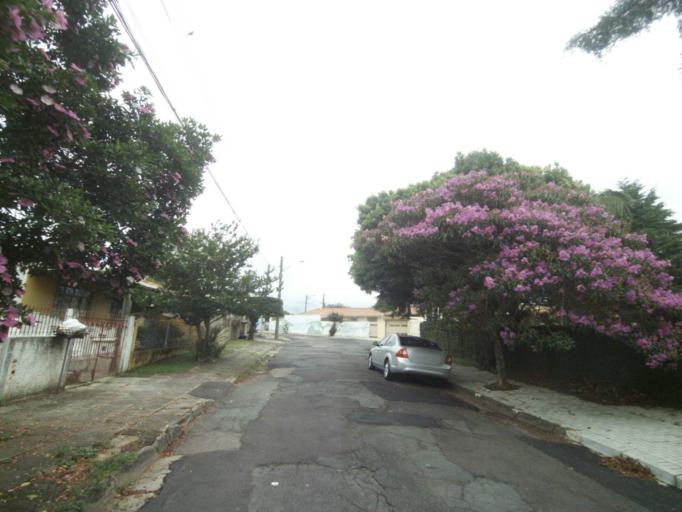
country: BR
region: Parana
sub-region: Curitiba
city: Curitiba
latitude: -25.4931
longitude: -49.2823
